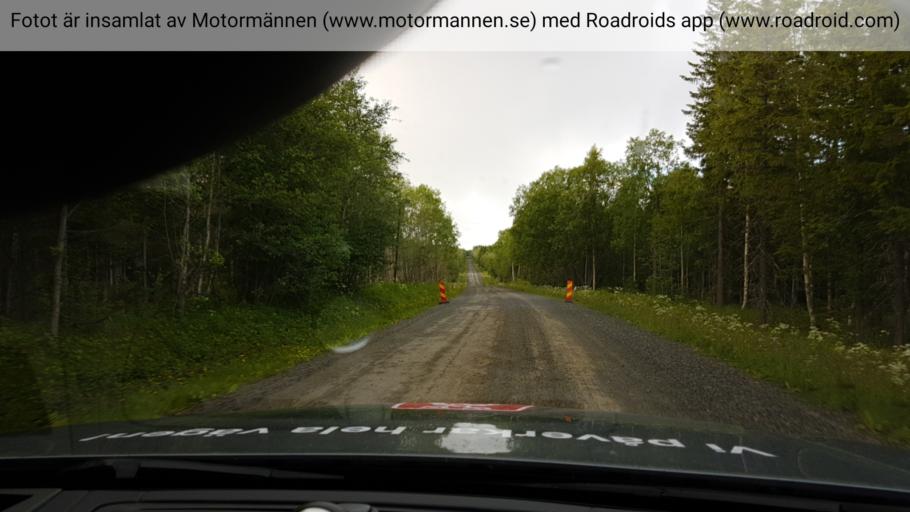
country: SE
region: Jaemtland
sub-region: Bergs Kommun
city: Hoverberg
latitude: 62.9626
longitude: 14.2369
